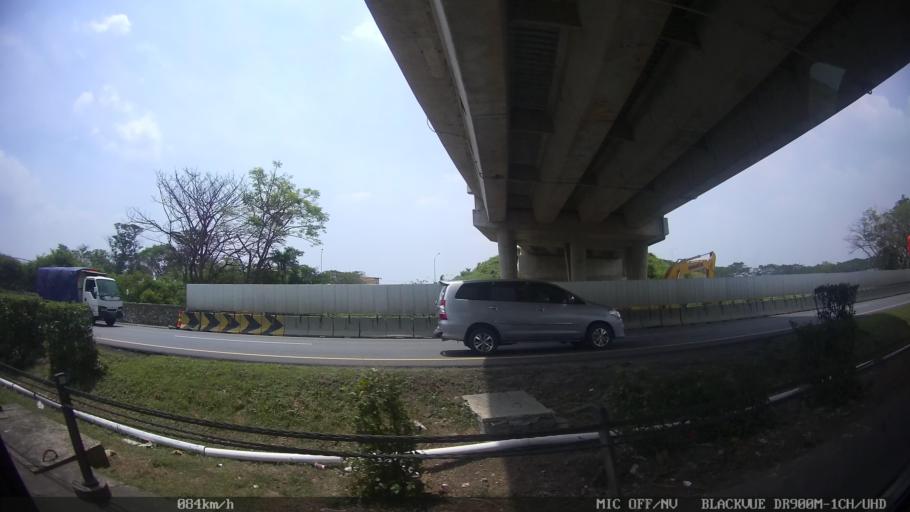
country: ID
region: Banten
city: Serang
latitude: -6.1386
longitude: 106.2452
